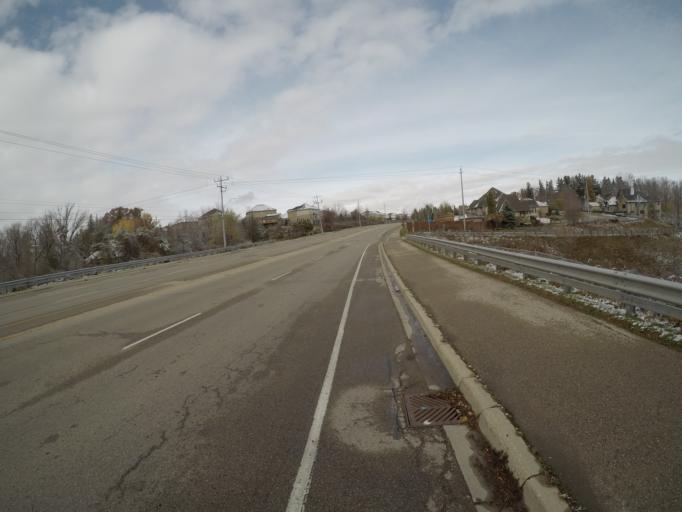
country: CA
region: Ontario
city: Waterloo
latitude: 43.5048
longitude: -80.4967
